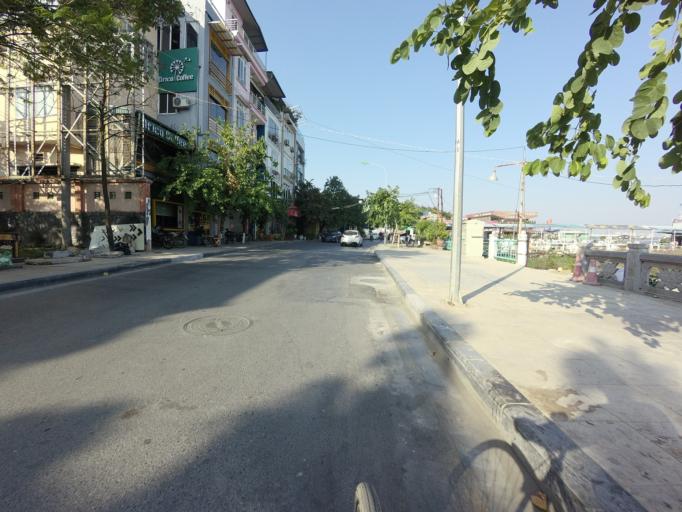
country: VN
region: Ha Noi
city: Hanoi
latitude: 21.0437
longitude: 105.8346
